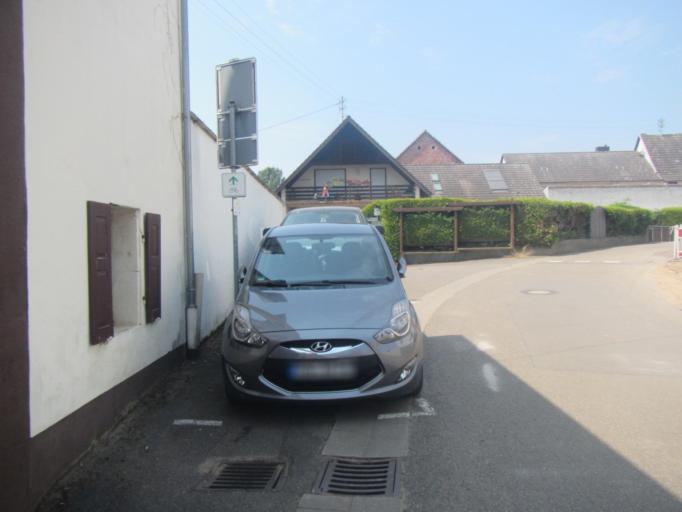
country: DE
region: Rheinland-Pfalz
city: Niederhorbach
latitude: 49.1159
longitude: 8.0300
